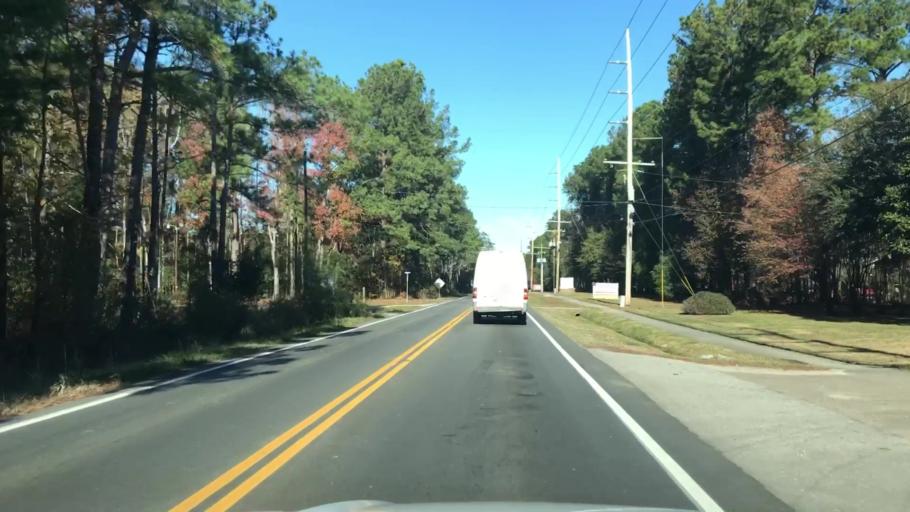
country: US
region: South Carolina
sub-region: Dorchester County
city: Summerville
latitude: 32.9985
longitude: -80.2297
